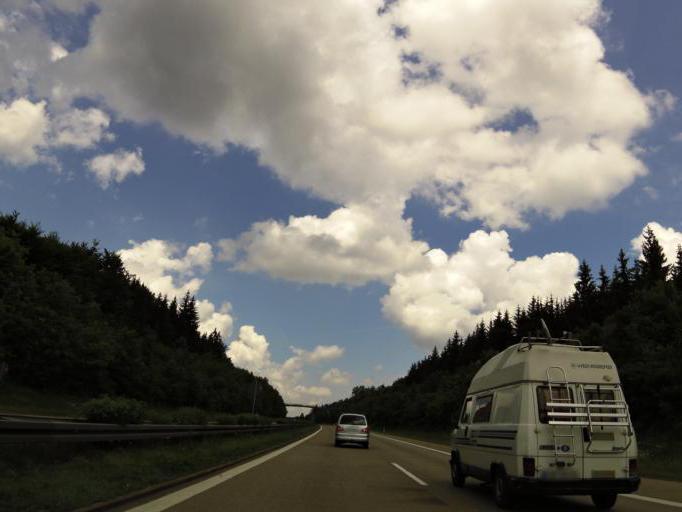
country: DE
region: Baden-Wuerttemberg
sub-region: Regierungsbezirk Stuttgart
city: Nattheim
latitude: 48.7022
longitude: 10.2158
